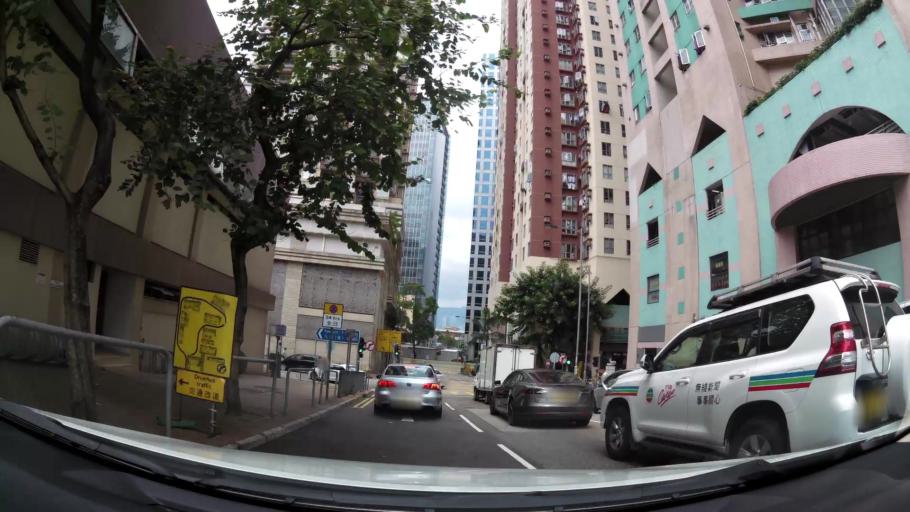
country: HK
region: Kowloon City
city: Kowloon
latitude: 22.2911
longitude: 114.2057
